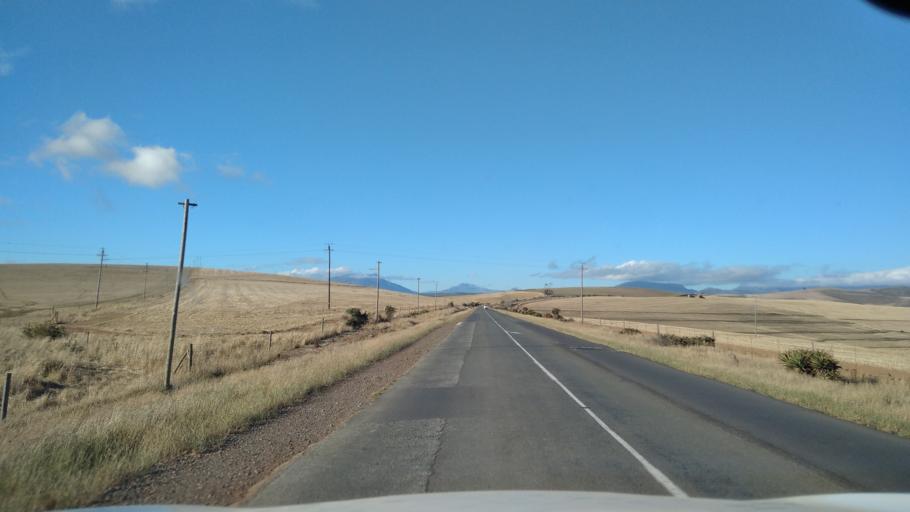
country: ZA
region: Western Cape
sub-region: Overberg District Municipality
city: Caledon
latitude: -34.1960
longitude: 19.2695
